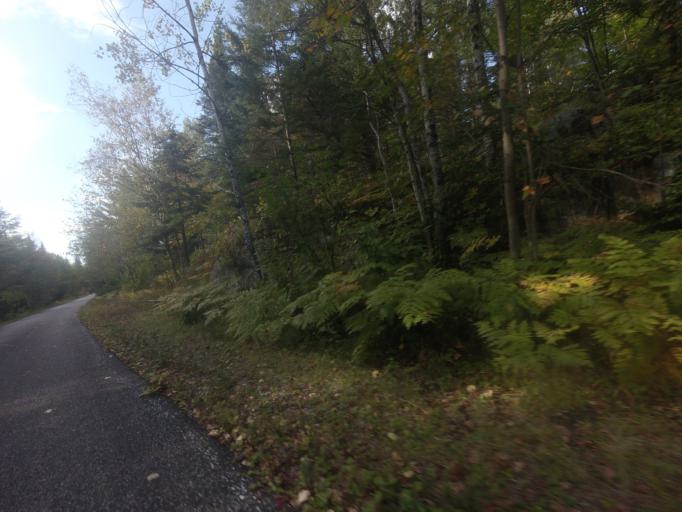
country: CA
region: Quebec
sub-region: Laurentides
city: Labelle
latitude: 46.3185
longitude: -74.7771
